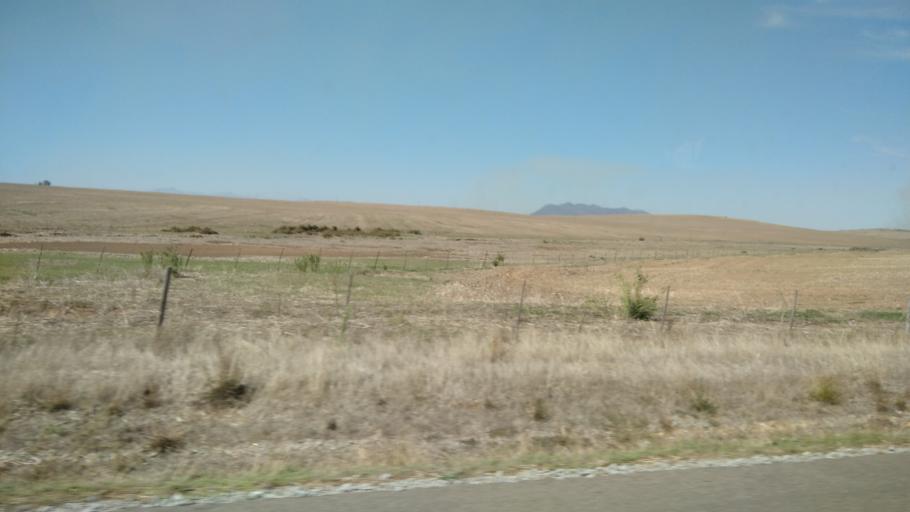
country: ZA
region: Western Cape
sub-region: West Coast District Municipality
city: Malmesbury
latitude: -33.3486
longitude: 18.6404
